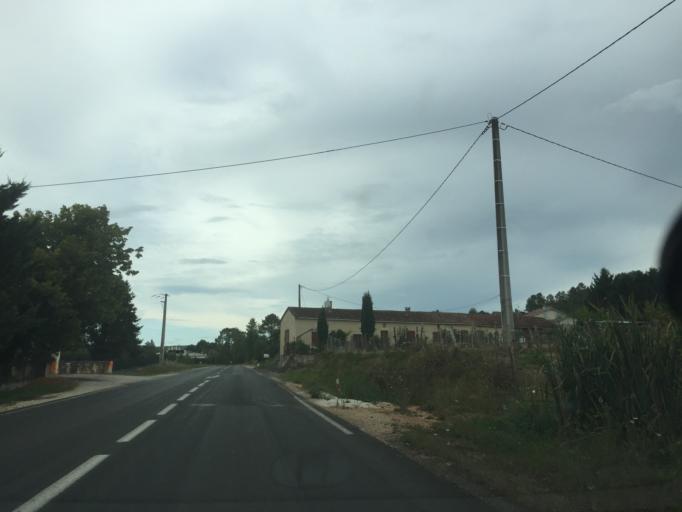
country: FR
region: Aquitaine
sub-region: Departement du Lot-et-Garonne
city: Fumel
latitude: 44.5096
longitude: 0.9492
